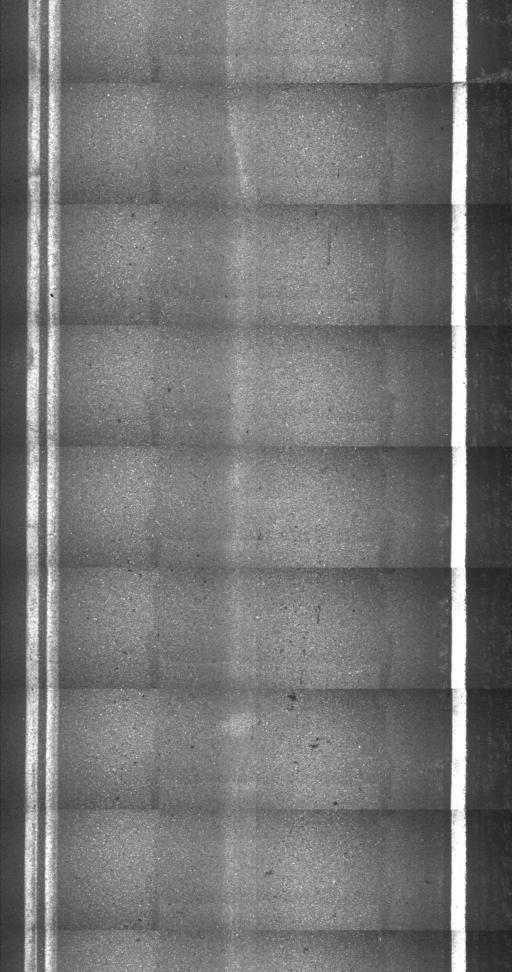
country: US
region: Vermont
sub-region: Caledonia County
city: Lyndonville
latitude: 44.7182
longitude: -71.8697
